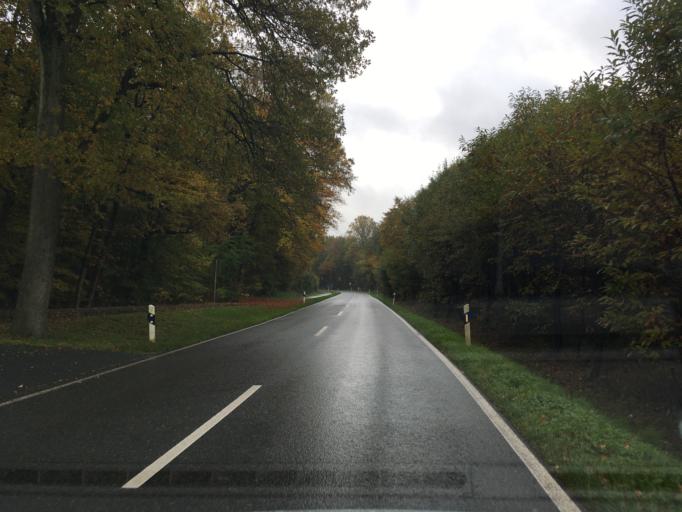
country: DE
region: North Rhine-Westphalia
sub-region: Regierungsbezirk Munster
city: Klein Reken
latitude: 51.8416
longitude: 7.0303
